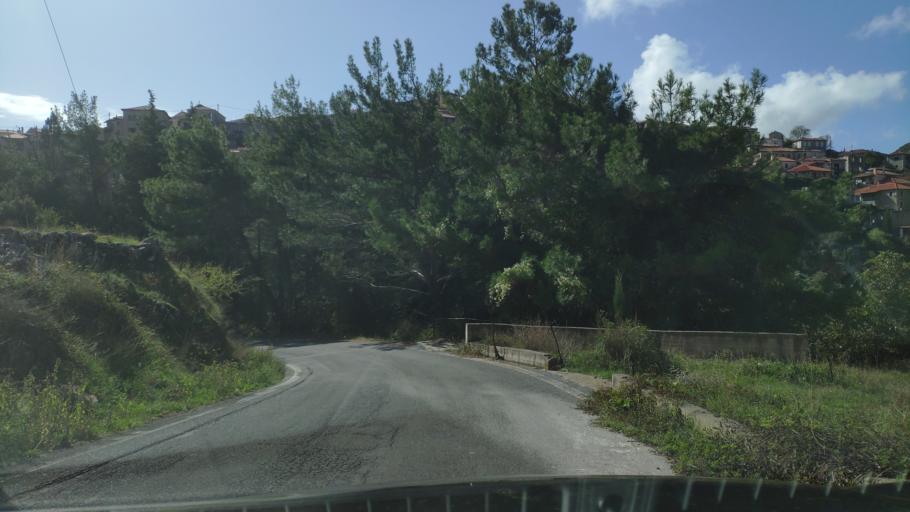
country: GR
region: Peloponnese
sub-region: Nomos Arkadias
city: Dimitsana
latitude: 37.5975
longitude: 22.0410
